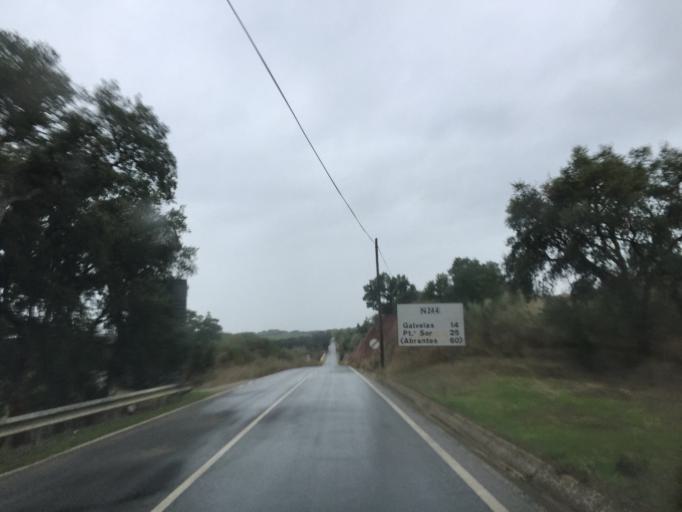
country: PT
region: Portalegre
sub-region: Avis
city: Avis
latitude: 39.0656
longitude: -7.8981
